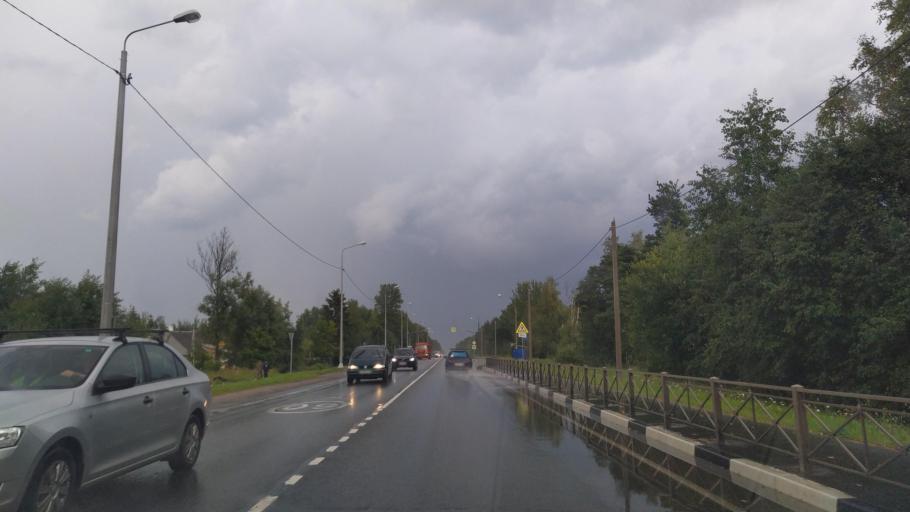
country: RU
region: Pskov
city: Pskov
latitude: 57.7616
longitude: 28.3867
